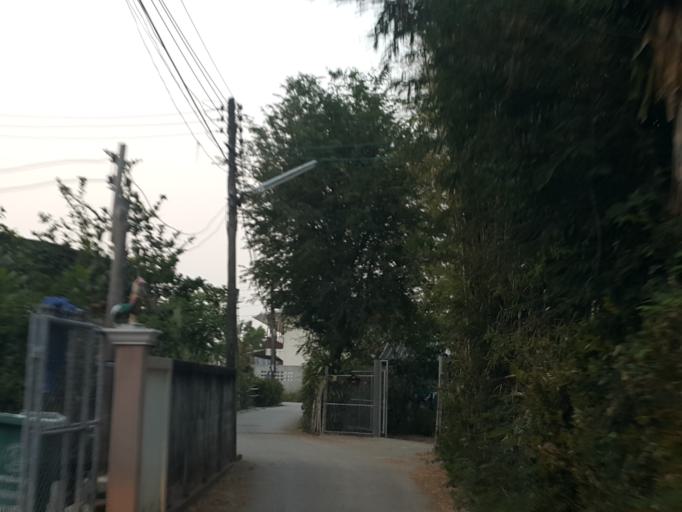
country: TH
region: Chiang Mai
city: San Kamphaeng
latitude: 18.7735
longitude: 99.0746
